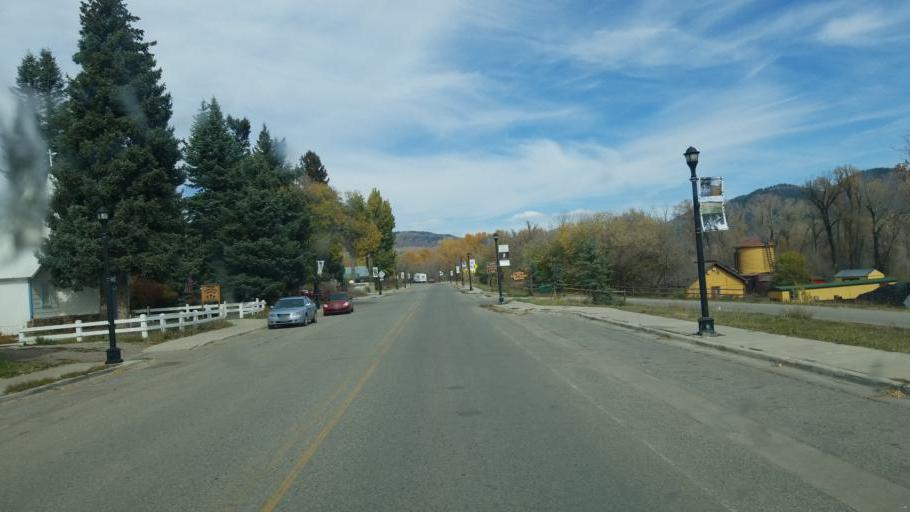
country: US
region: New Mexico
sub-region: Rio Arriba County
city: Chama
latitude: 36.9040
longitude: -106.5786
